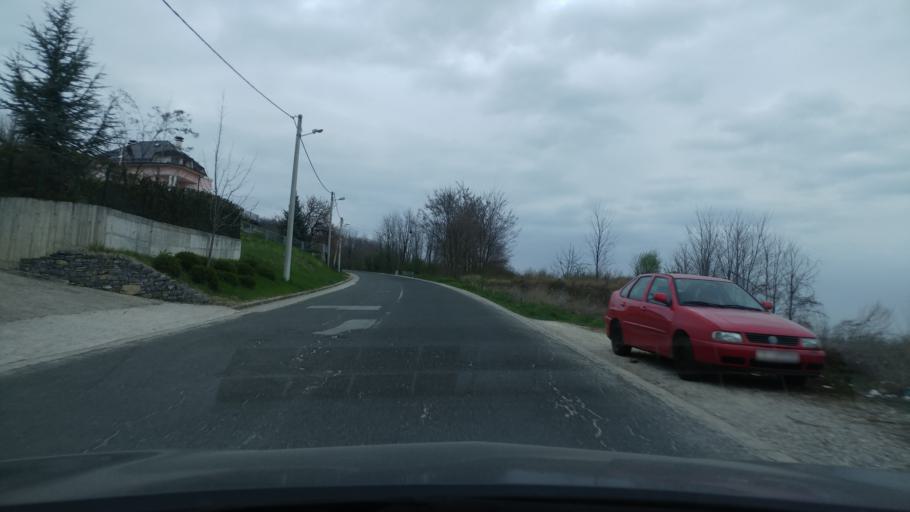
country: HR
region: Grad Zagreb
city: Stenjevec
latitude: 45.8364
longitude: 15.8818
